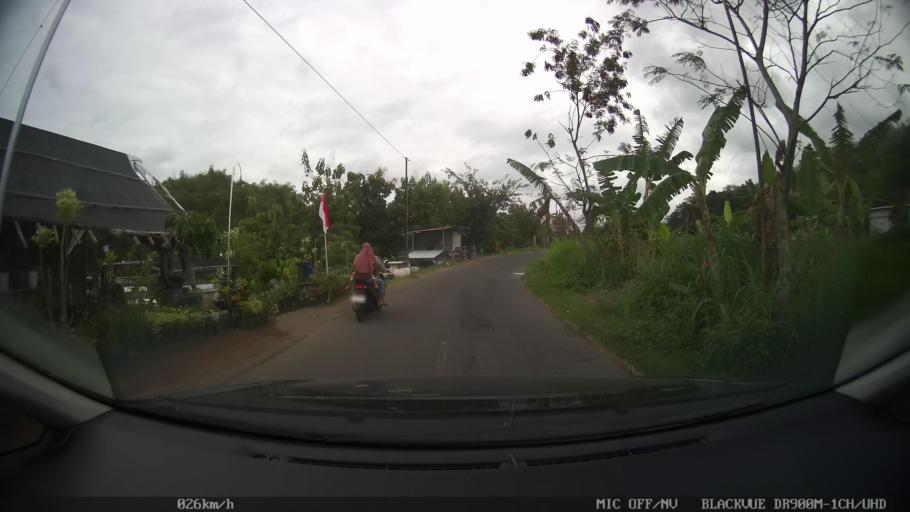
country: ID
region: Daerah Istimewa Yogyakarta
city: Sewon
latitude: -7.8633
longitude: 110.4212
